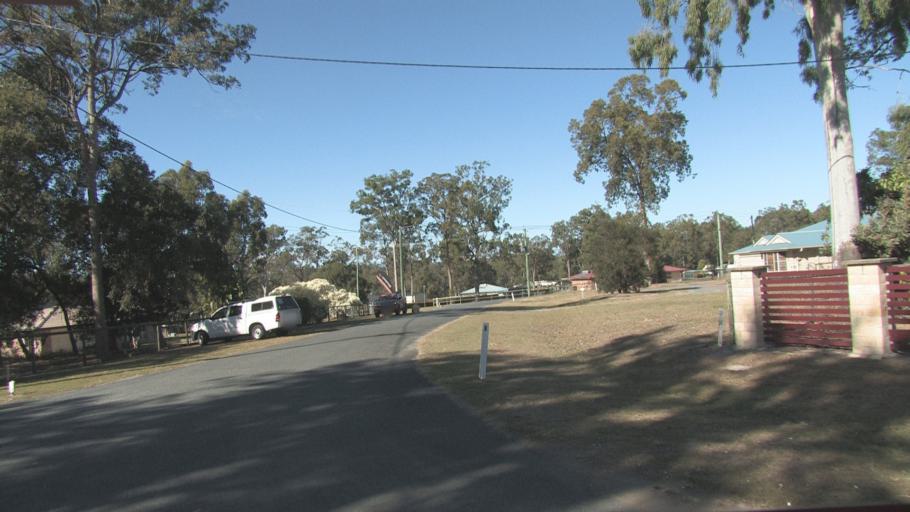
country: AU
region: Queensland
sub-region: Logan
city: Chambers Flat
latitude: -27.7733
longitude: 153.0788
